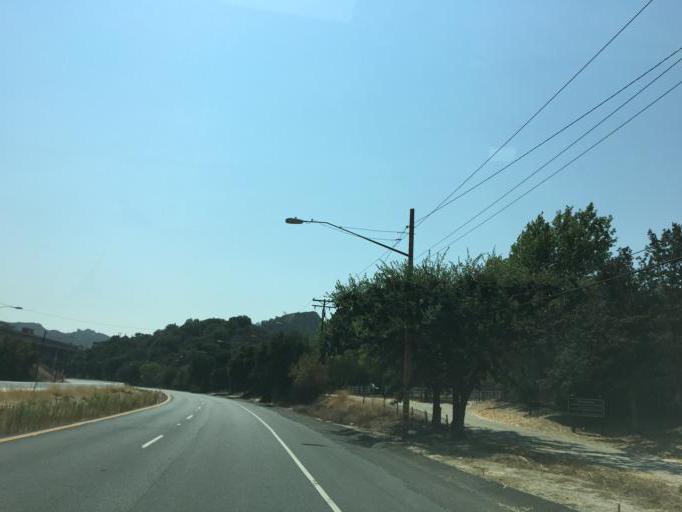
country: US
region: California
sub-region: Los Angeles County
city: Santa Clarita
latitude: 34.3512
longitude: -118.5474
